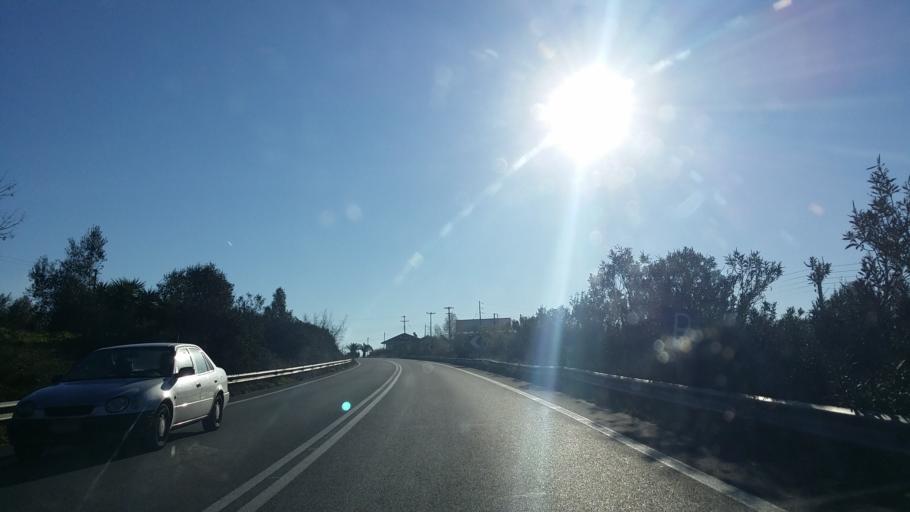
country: GR
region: West Greece
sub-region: Nomos Aitolias kai Akarnanias
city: Fitiai
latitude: 38.6904
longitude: 21.2268
